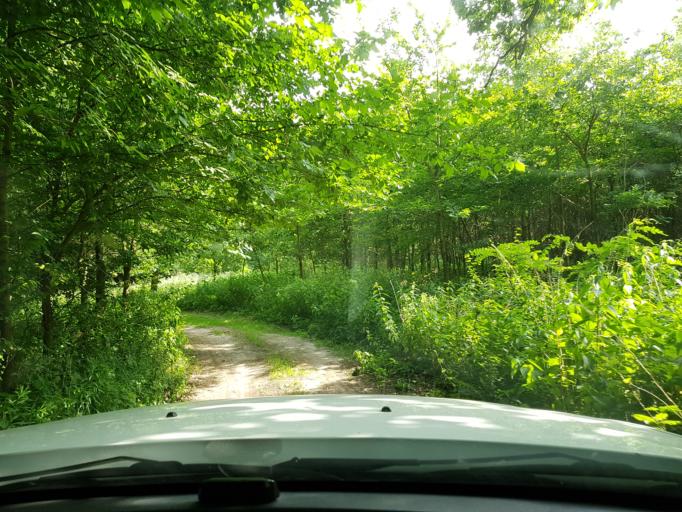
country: PL
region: West Pomeranian Voivodeship
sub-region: Powiat gryfinski
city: Moryn
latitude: 52.9220
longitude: 14.3643
